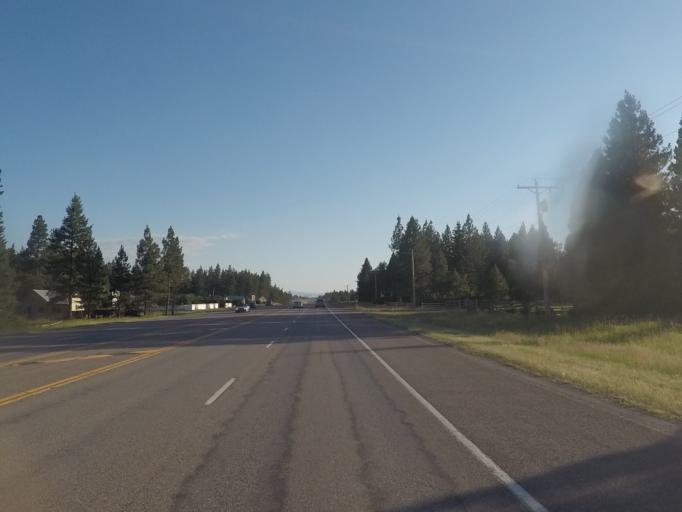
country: US
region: Montana
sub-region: Flathead County
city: Columbia Falls
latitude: 48.3789
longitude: -114.1273
